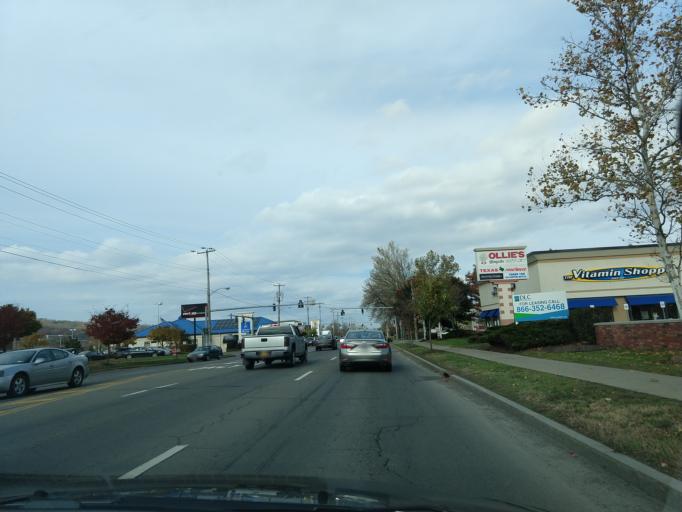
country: US
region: New York
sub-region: Tompkins County
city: South Hill
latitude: 42.4309
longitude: -76.5079
